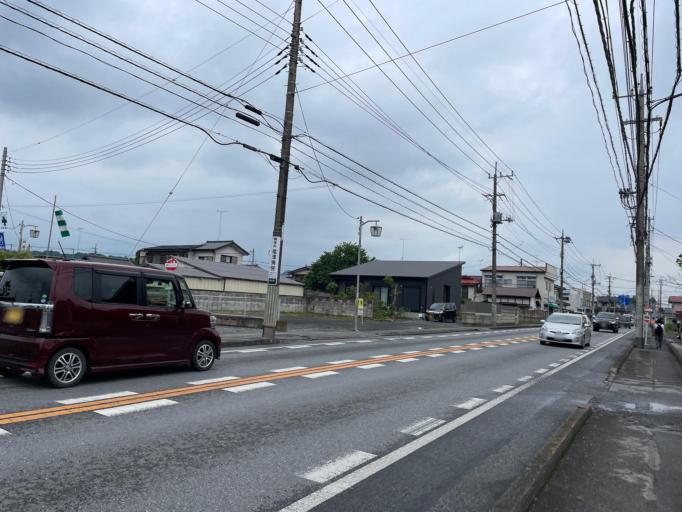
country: JP
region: Tochigi
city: Kanuma
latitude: 36.5373
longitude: 139.7471
